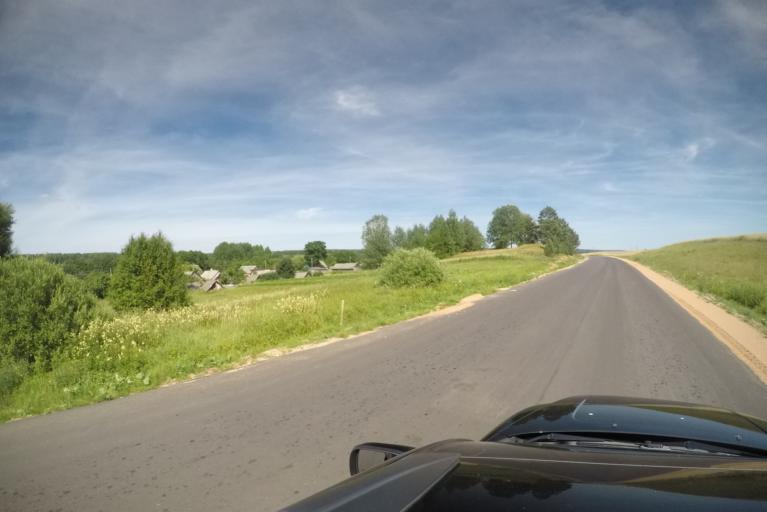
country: BY
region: Grodnenskaya
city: Hal'shany
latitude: 54.2585
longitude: 25.9784
